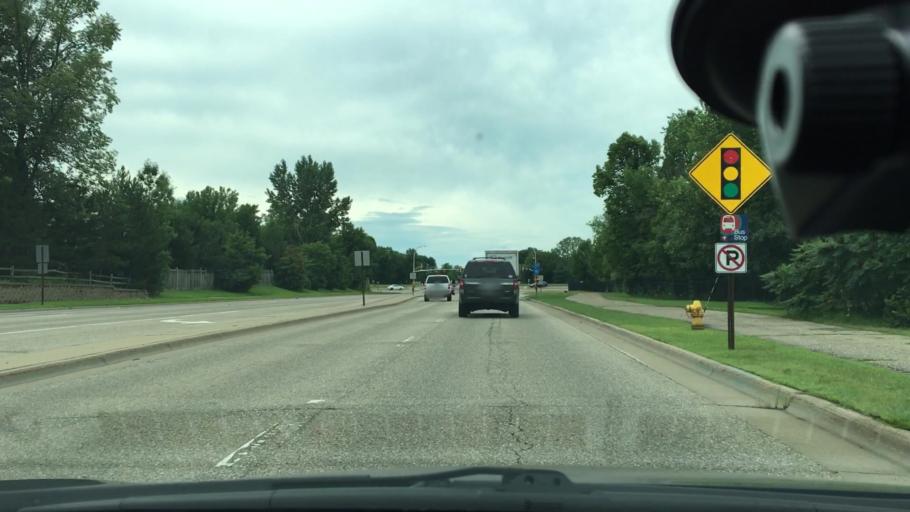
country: US
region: Minnesota
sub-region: Hennepin County
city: Maple Grove
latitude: 45.0642
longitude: -93.4359
